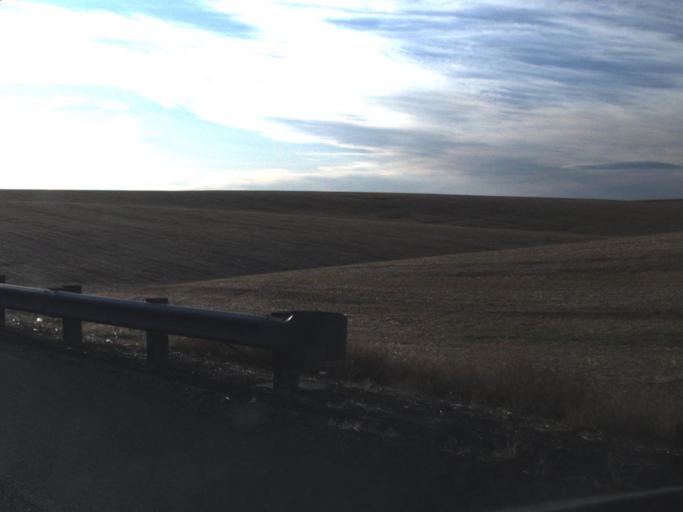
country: US
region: Washington
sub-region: Walla Walla County
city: Walla Walla East
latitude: 46.1139
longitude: -118.2250
